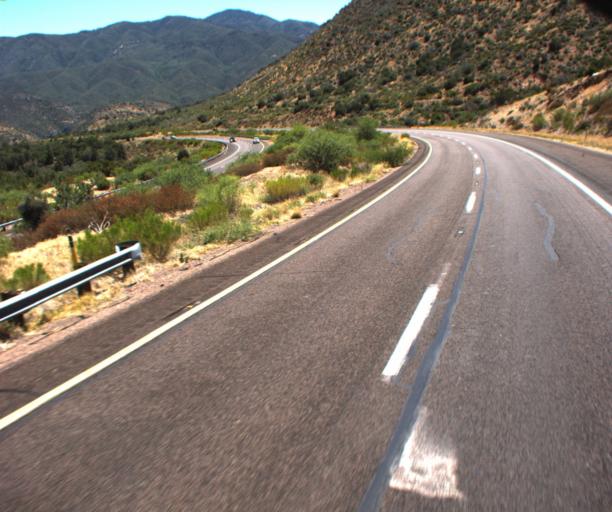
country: US
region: Arizona
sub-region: Gila County
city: Tonto Basin
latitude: 33.9824
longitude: -111.3851
